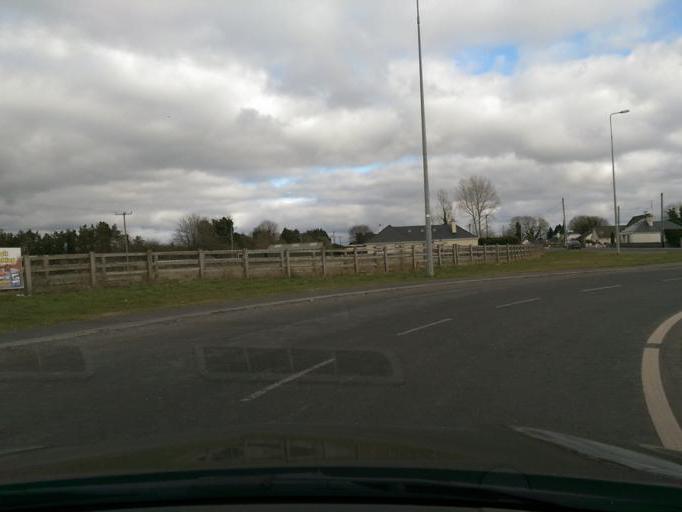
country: IE
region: Connaught
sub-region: County Galway
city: Ballinasloe
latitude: 53.3283
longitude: -8.1752
